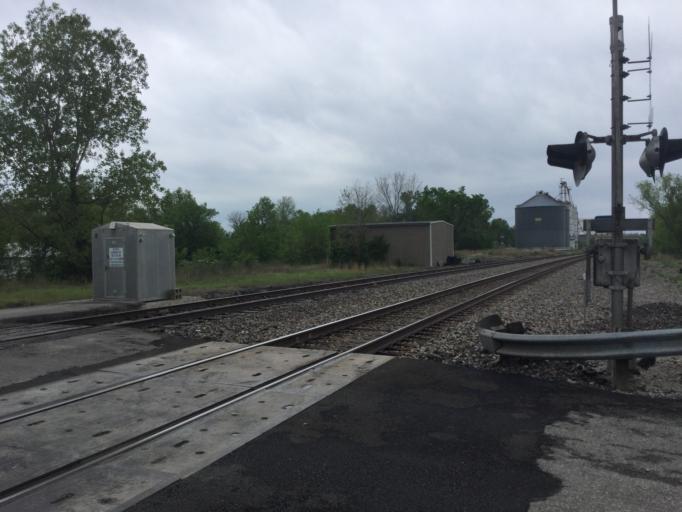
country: US
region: Kansas
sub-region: Labette County
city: Chetopa
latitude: 37.0326
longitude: -95.1023
